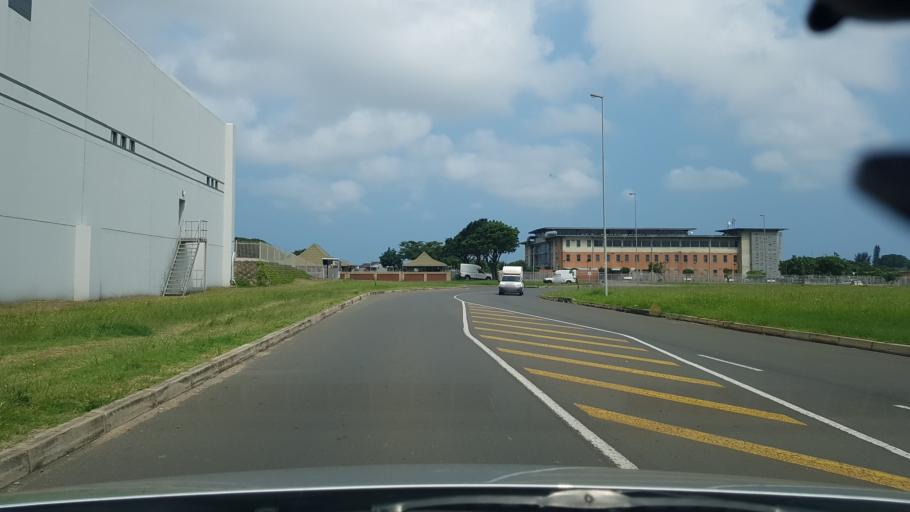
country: ZA
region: KwaZulu-Natal
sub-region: uThungulu District Municipality
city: Richards Bay
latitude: -28.7563
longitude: 32.0481
